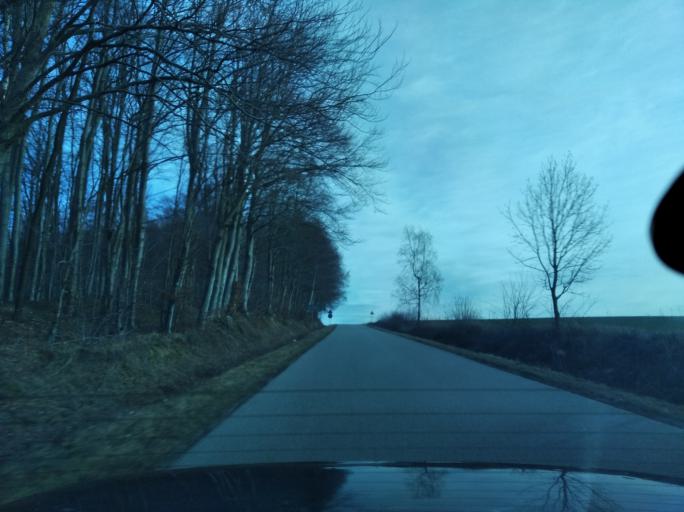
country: PL
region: Subcarpathian Voivodeship
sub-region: Powiat ropczycko-sedziszowski
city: Wielopole Skrzynskie
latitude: 49.9401
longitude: 21.6912
